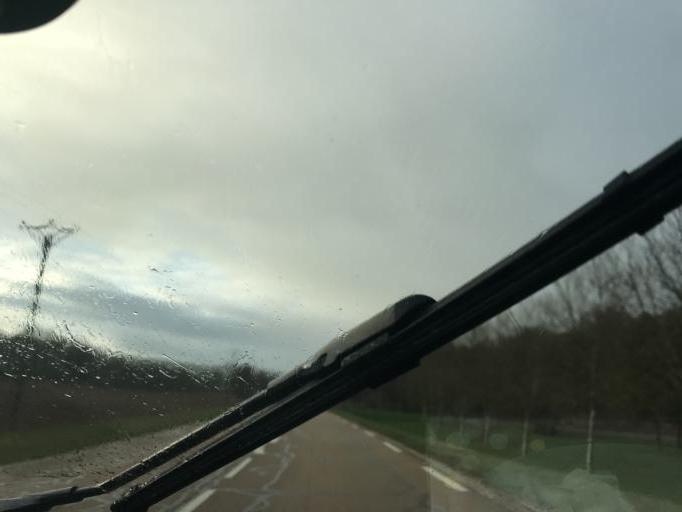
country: FR
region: Bourgogne
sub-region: Departement de l'Yonne
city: Fontenailles
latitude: 47.6211
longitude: 3.4960
